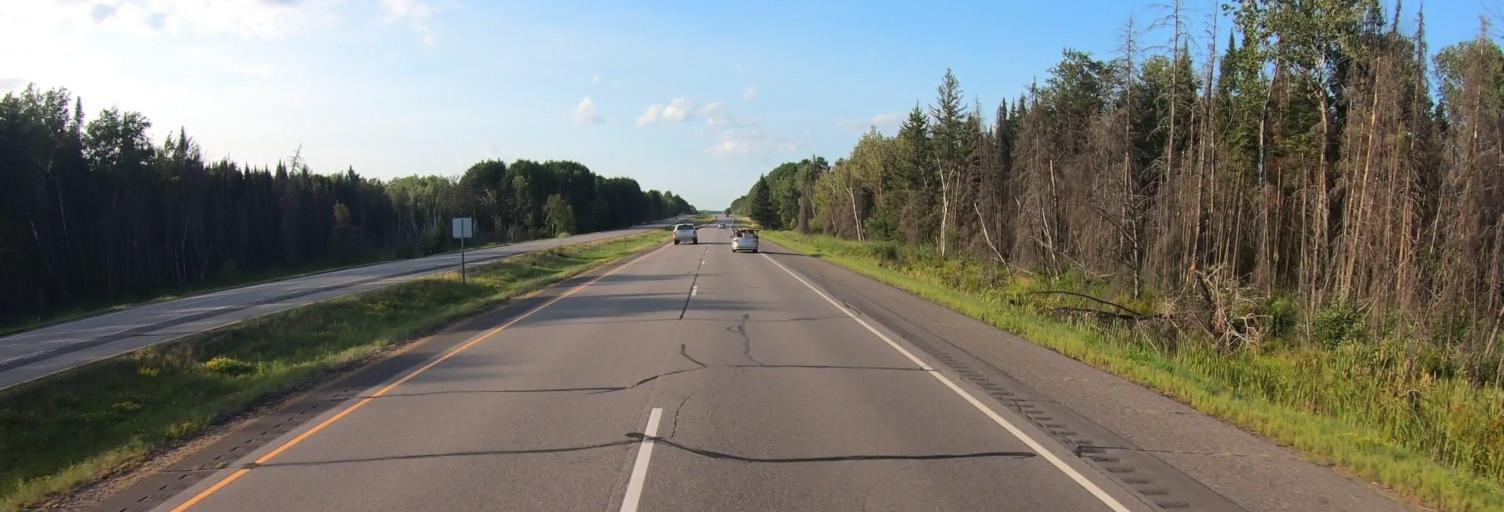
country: US
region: Minnesota
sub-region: Saint Louis County
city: Eveleth
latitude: 47.4093
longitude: -92.5207
